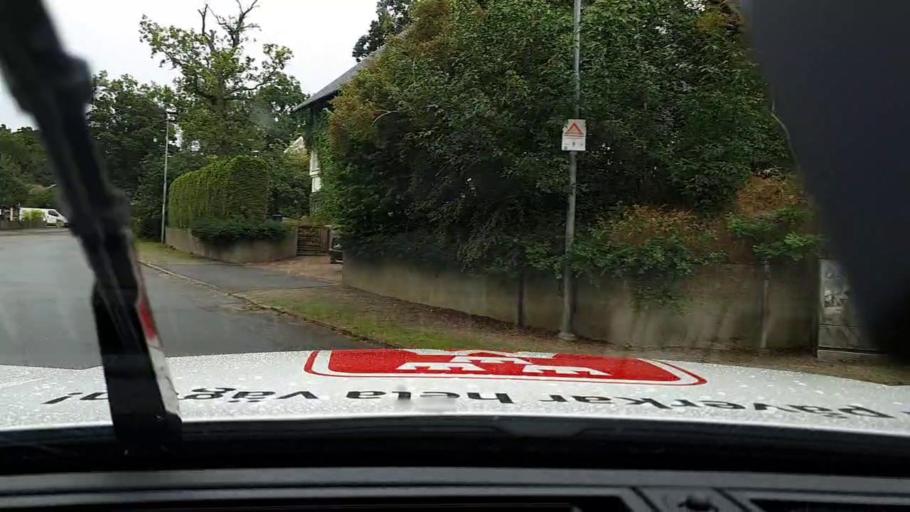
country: SE
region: Skane
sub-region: Hassleholms Kommun
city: Hassleholm
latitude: 56.1689
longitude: 13.7726
